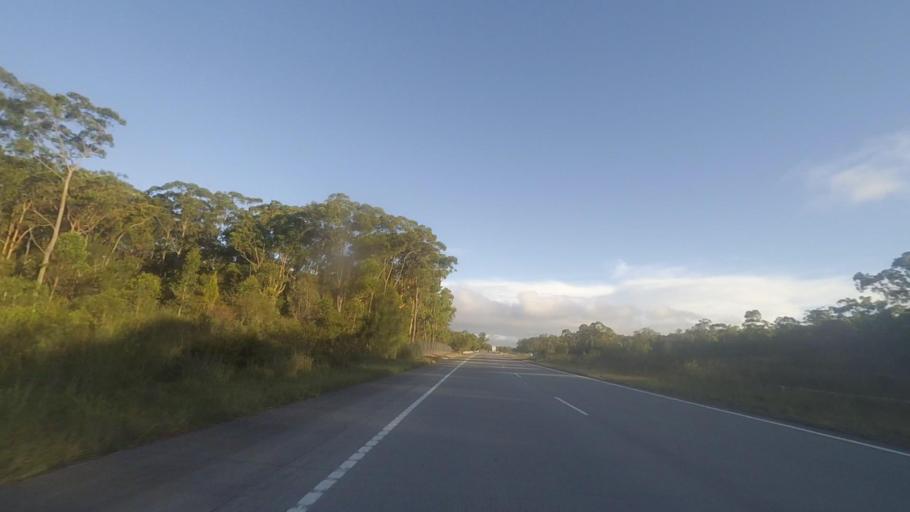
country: AU
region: New South Wales
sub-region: Great Lakes
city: Bulahdelah
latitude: -32.4926
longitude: 152.2020
